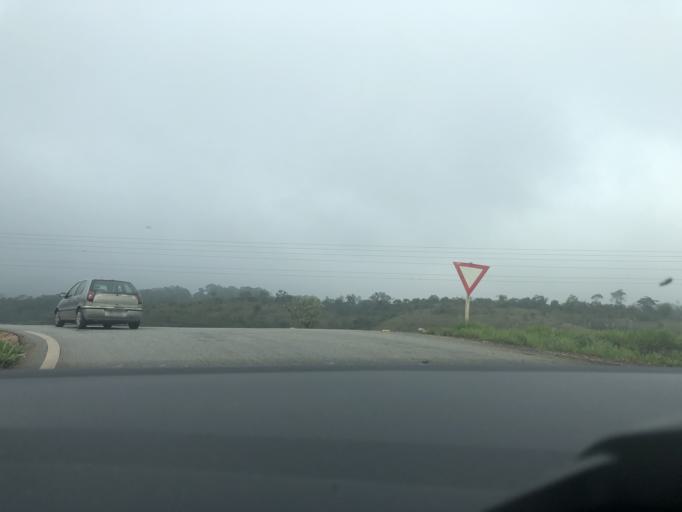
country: BR
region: Minas Gerais
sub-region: Congonhas
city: Congonhas
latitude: -20.5836
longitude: -43.9459
